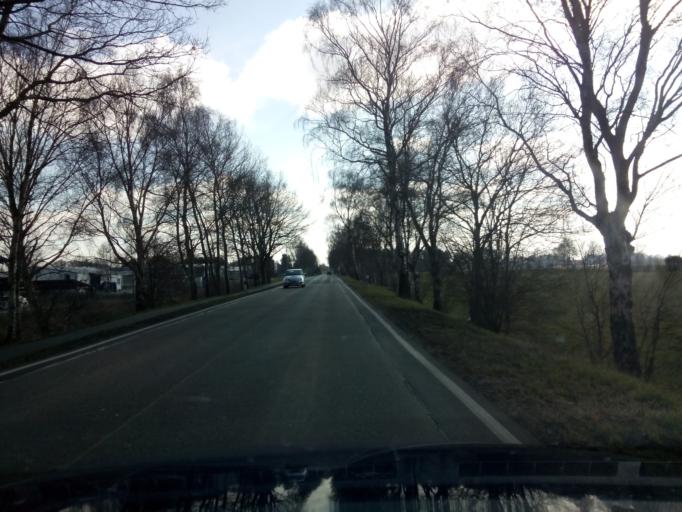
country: DE
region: Lower Saxony
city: Grasberg
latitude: 53.1930
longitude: 8.9785
